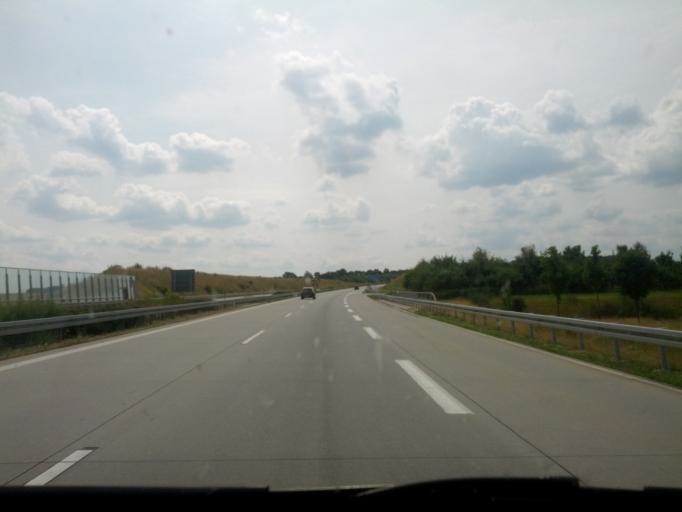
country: DE
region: Saxony
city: Dohma
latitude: 50.8989
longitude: 13.8920
